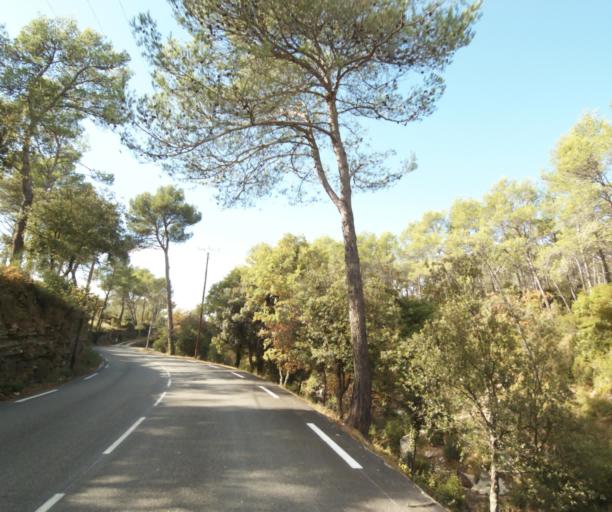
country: FR
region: Provence-Alpes-Cote d'Azur
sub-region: Departement des Bouches-du-Rhone
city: Ceyreste
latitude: 43.2342
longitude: 5.6681
